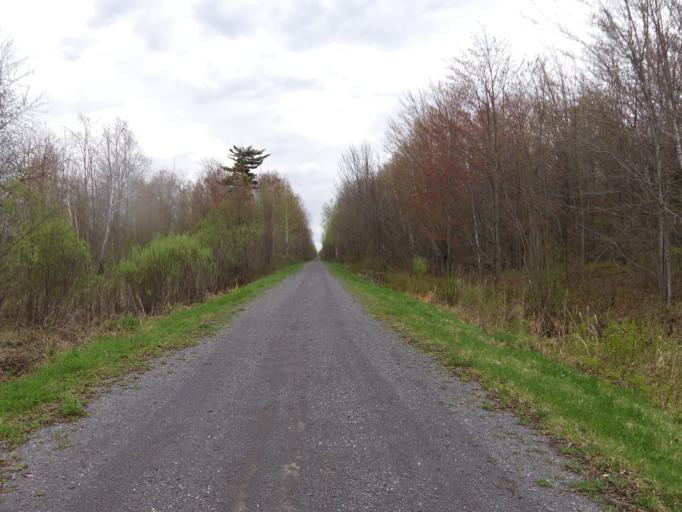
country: CA
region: Quebec
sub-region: Outaouais
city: Papineauville
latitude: 45.5166
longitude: -74.9409
